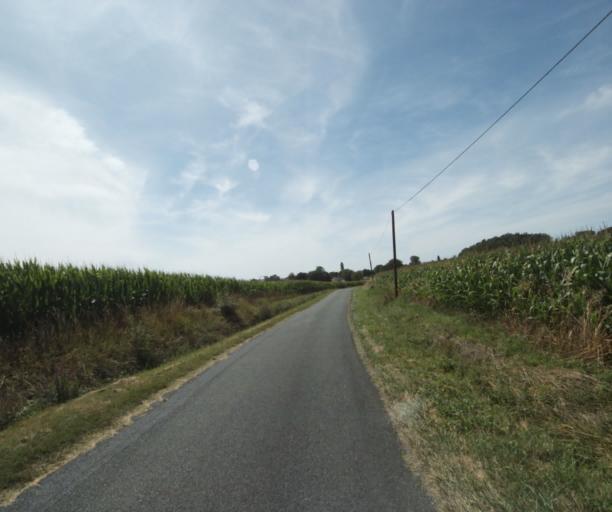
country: FR
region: Midi-Pyrenees
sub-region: Departement du Tarn
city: Puylaurens
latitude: 43.5255
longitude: 2.0158
